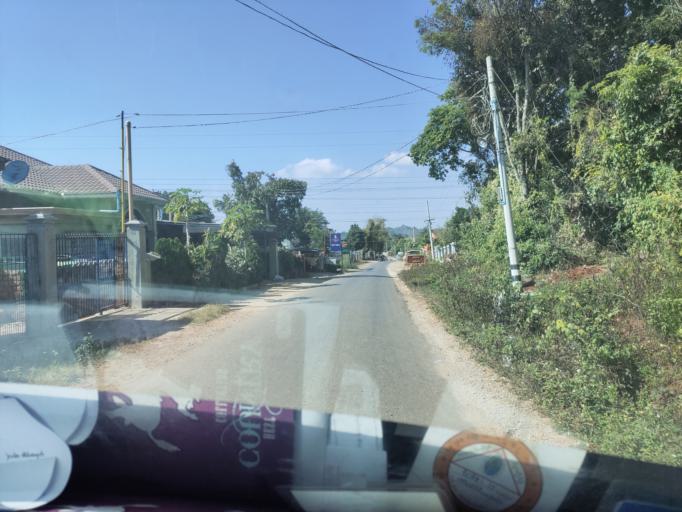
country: MM
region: Mandalay
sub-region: Pyin Oo Lwin District
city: Pyin Oo Lwin
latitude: 21.9522
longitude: 96.3963
